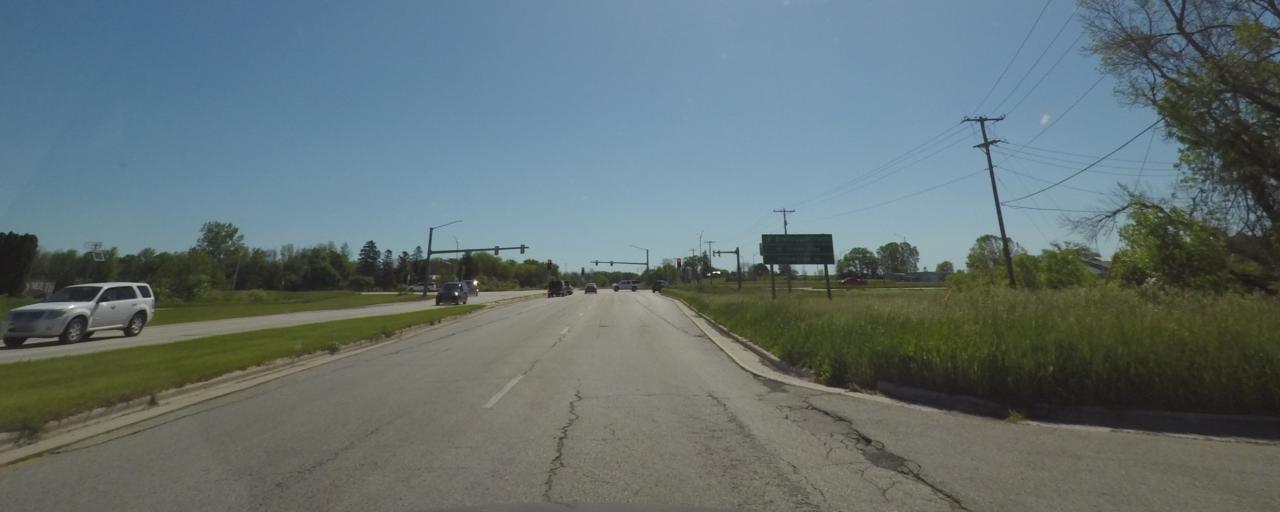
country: US
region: Wisconsin
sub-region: Sheboygan County
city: Plymouth
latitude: 43.7471
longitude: -87.9430
